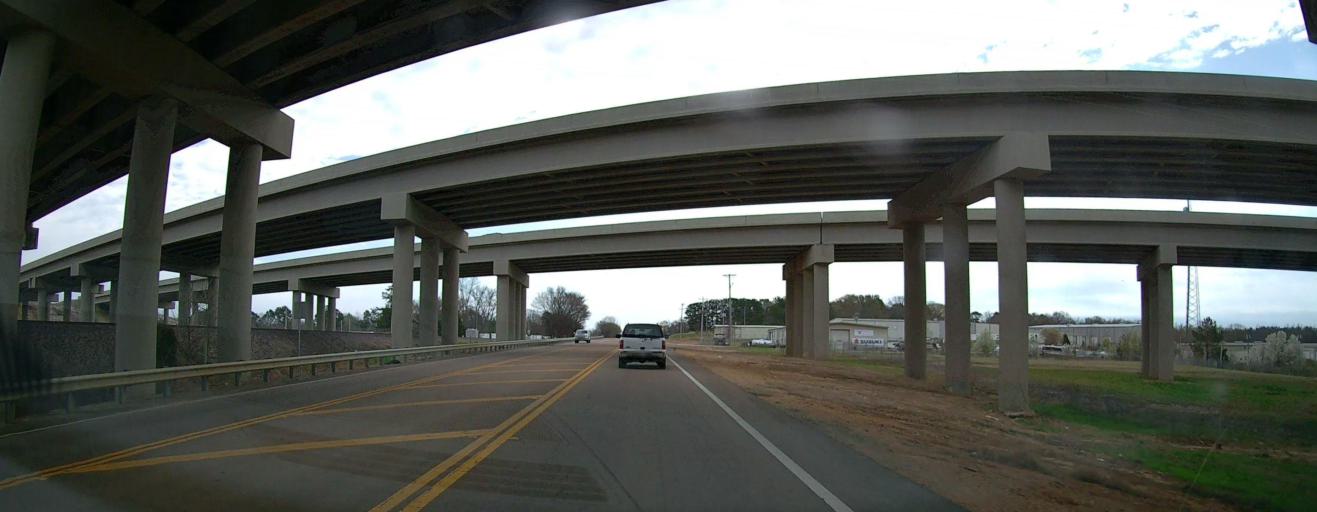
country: US
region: Mississippi
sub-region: Marshall County
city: Byhalia
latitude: 34.8837
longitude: -89.7179
